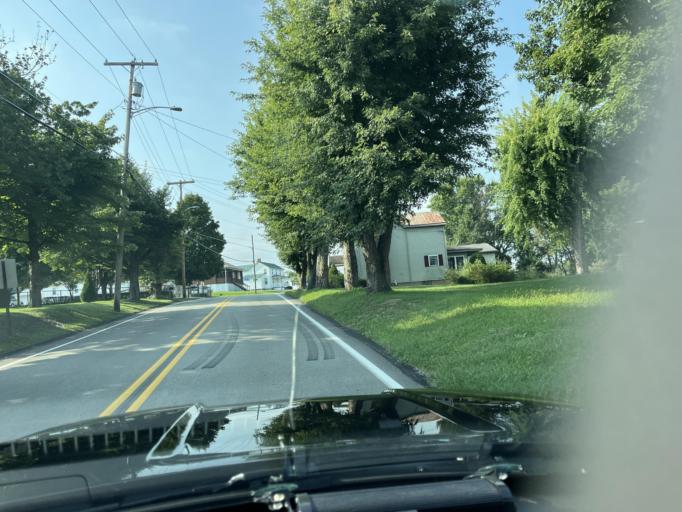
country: US
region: Pennsylvania
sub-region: Fayette County
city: Hopwood
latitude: 39.8642
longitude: -79.7088
